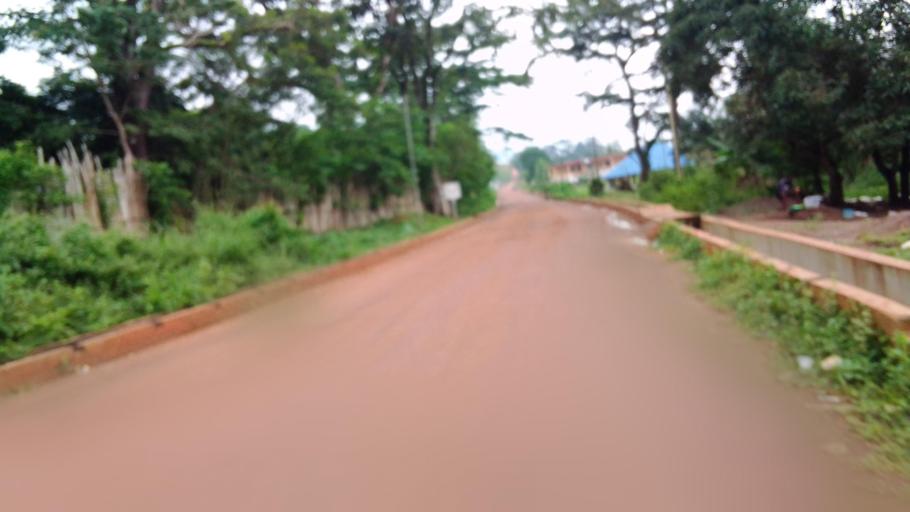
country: SL
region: Eastern Province
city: Kenema
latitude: 7.8876
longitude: -11.1919
